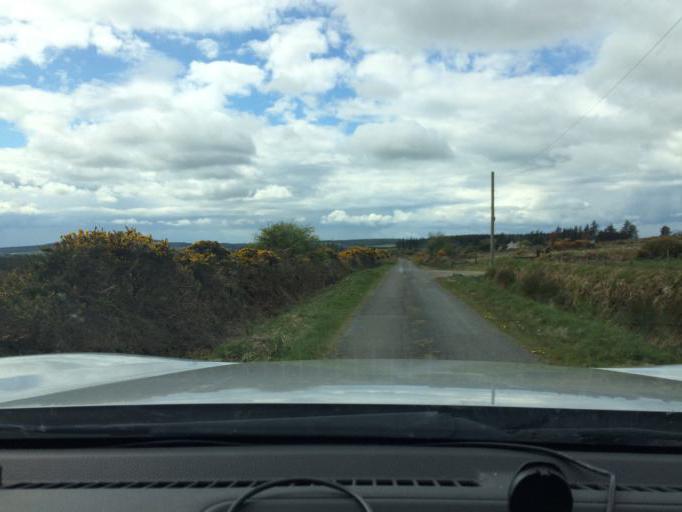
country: IE
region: Munster
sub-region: Waterford
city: Dungarvan
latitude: 52.0394
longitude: -7.6292
